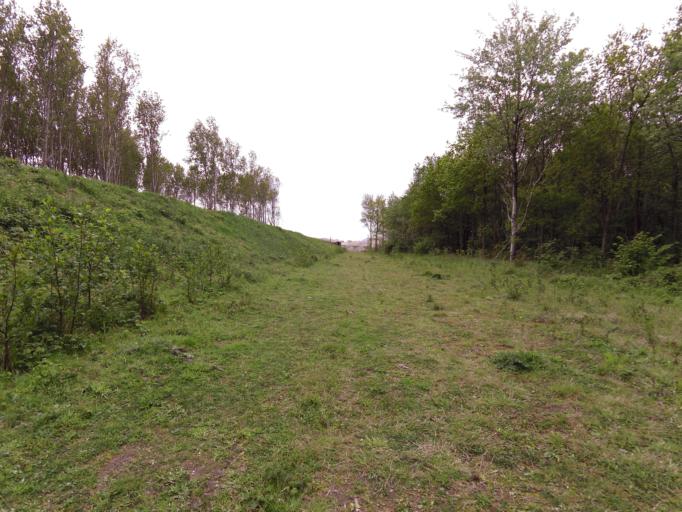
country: NL
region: South Holland
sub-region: Gemeente Goeree-Overflakkee
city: Ouddorp
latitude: 51.7837
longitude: 3.8878
